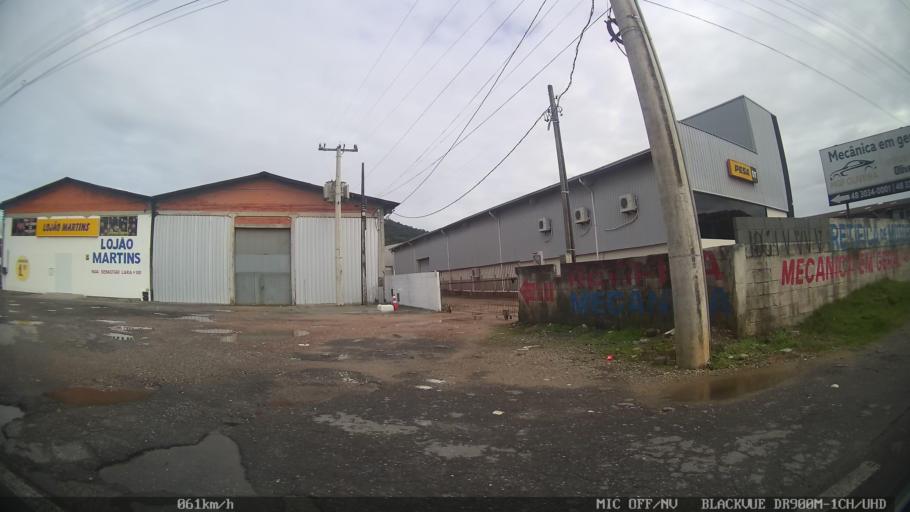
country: BR
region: Santa Catarina
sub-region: Biguacu
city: Biguacu
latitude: -27.4967
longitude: -48.6573
